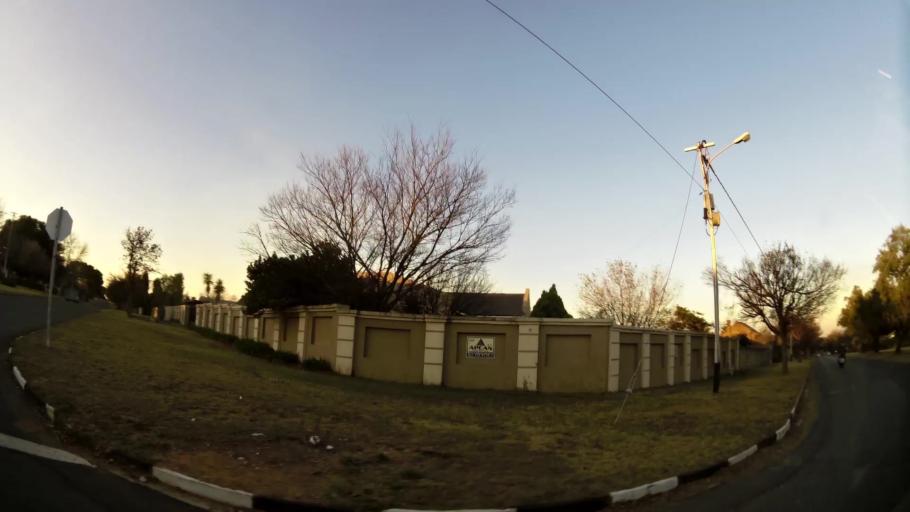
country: ZA
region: Gauteng
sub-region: City of Johannesburg Metropolitan Municipality
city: Roodepoort
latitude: -26.1541
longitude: 27.8817
